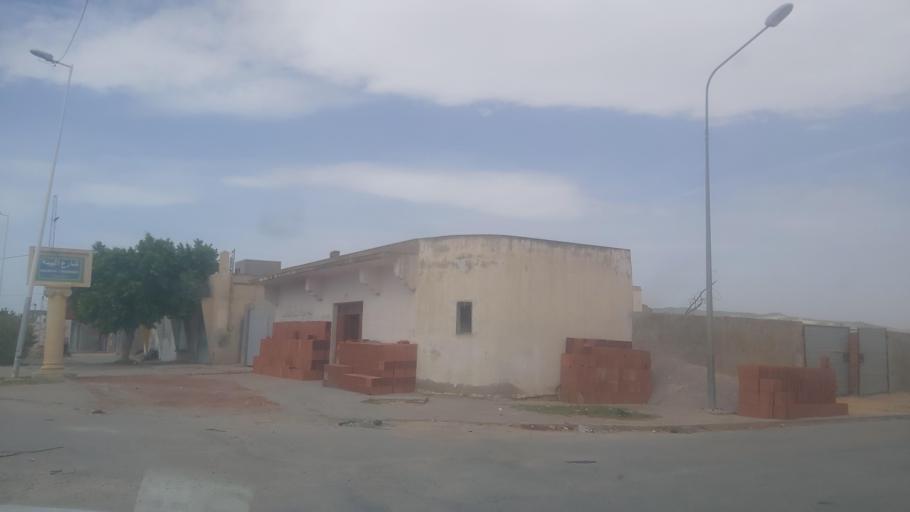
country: TN
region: Silyanah
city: Bu `Aradah
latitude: 36.3509
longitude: 9.6345
